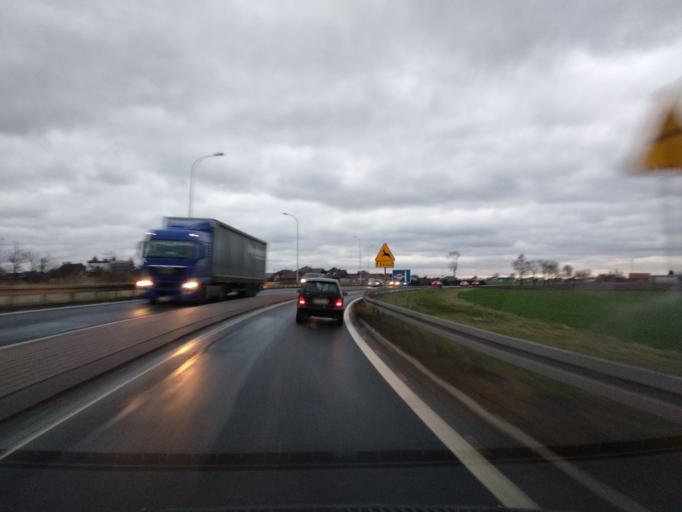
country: PL
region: Greater Poland Voivodeship
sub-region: Powiat koninski
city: Rychwal
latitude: 52.0667
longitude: 18.1634
